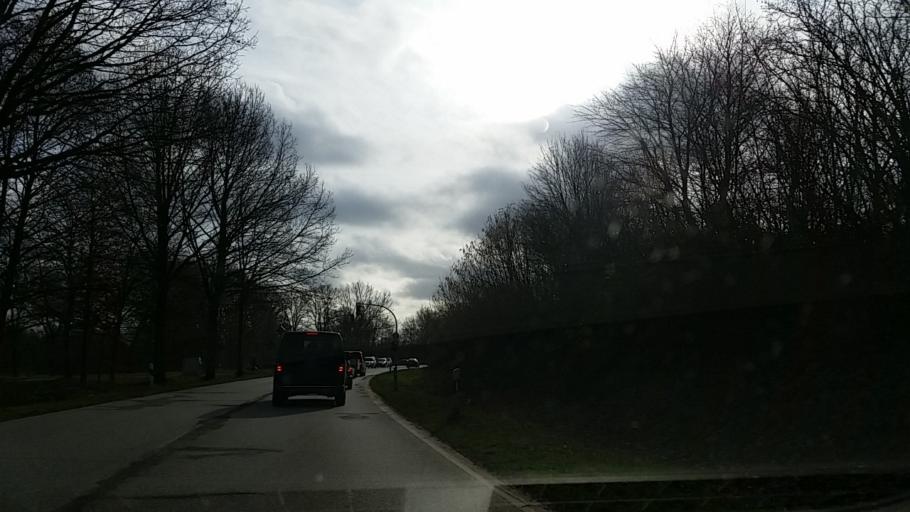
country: DE
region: Schleswig-Holstein
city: Bornsen
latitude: 53.4951
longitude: 10.2711
